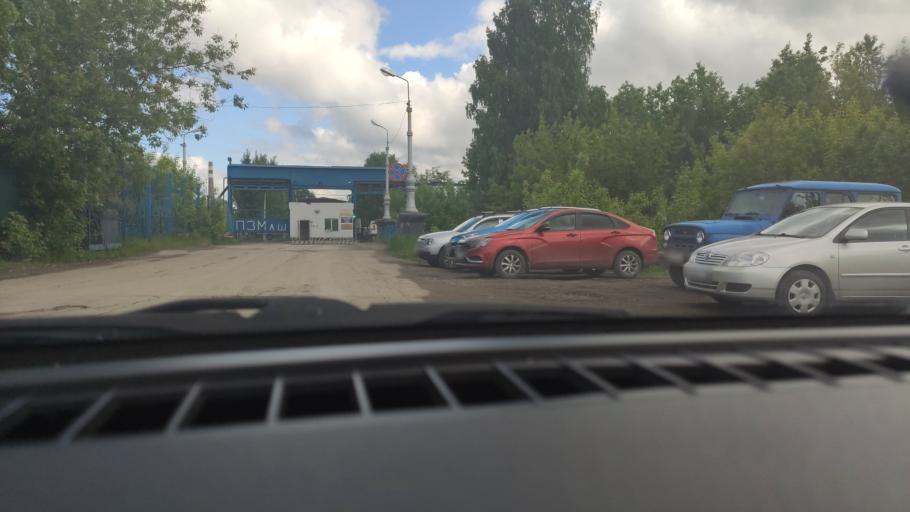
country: RU
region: Perm
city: Perm
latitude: 58.0595
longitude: 56.3271
